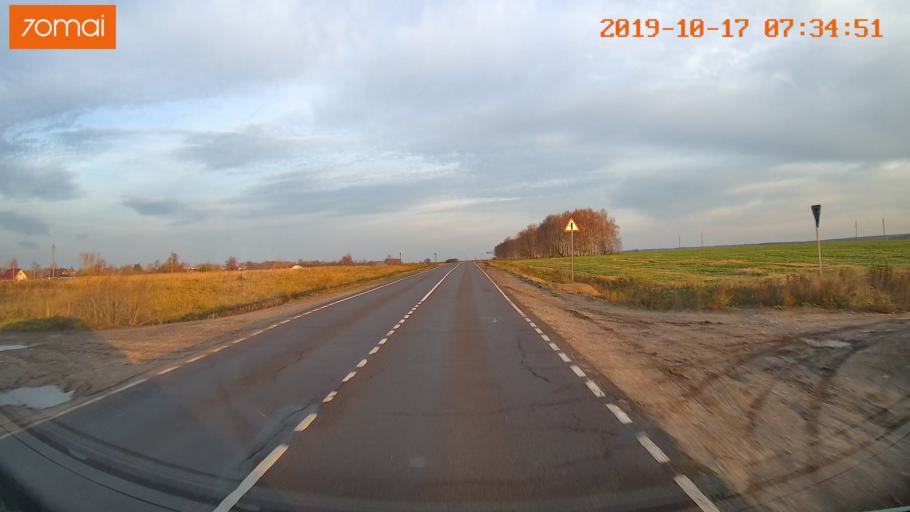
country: RU
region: Ivanovo
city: Gavrilov Posad
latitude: 56.4207
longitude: 39.9355
